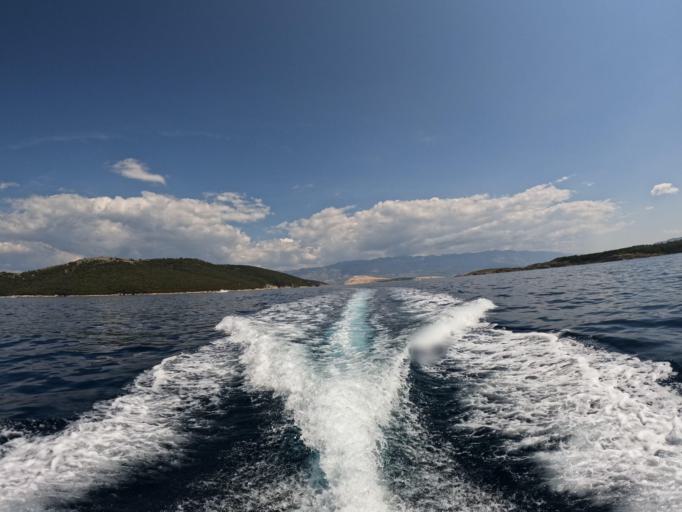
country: HR
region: Primorsko-Goranska
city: Lopar
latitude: 44.8563
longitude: 14.7364
